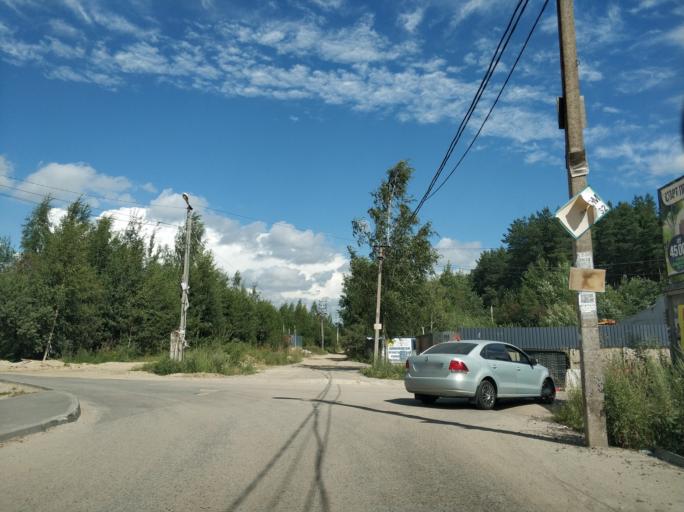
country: RU
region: Leningrad
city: Vsevolozhsk
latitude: 60.0228
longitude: 30.6097
